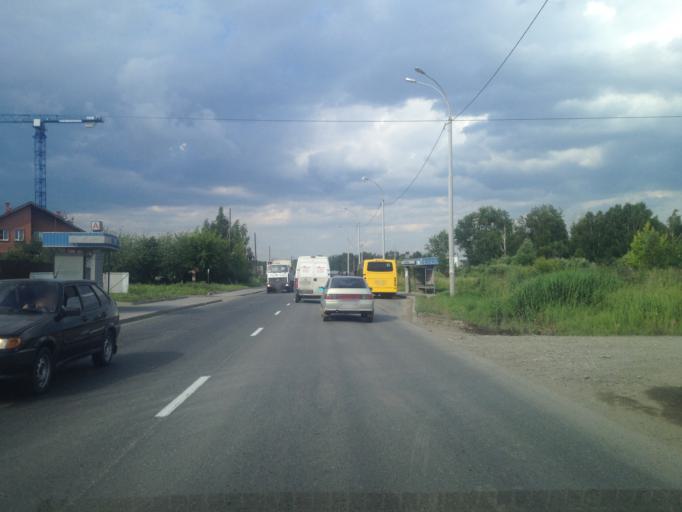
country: RU
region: Sverdlovsk
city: Shirokaya Rechka
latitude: 56.8073
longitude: 60.4966
